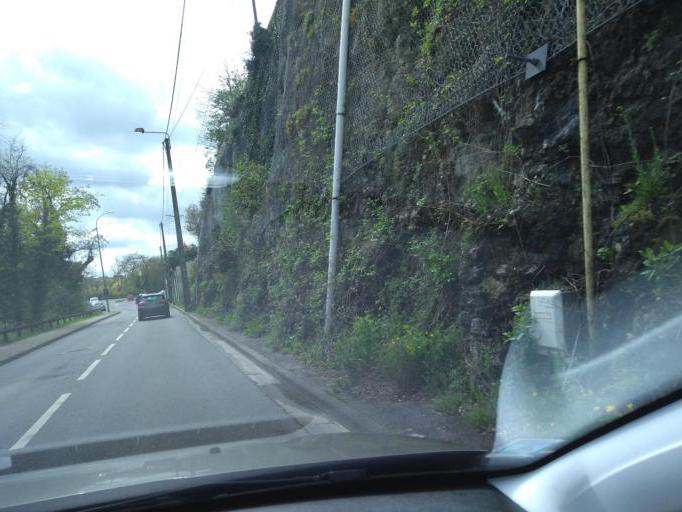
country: FR
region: Poitou-Charentes
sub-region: Departement de la Vienne
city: Poitiers
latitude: 46.5800
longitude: 0.3302
